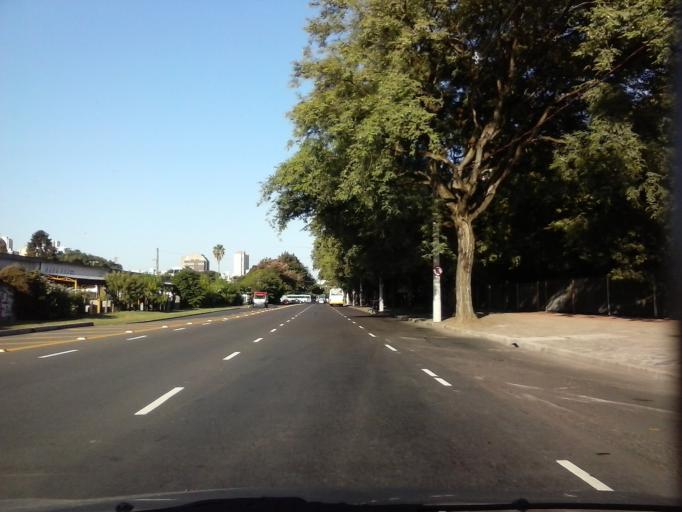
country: BR
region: Rio Grande do Sul
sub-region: Porto Alegre
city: Porto Alegre
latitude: -30.0370
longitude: -51.2398
